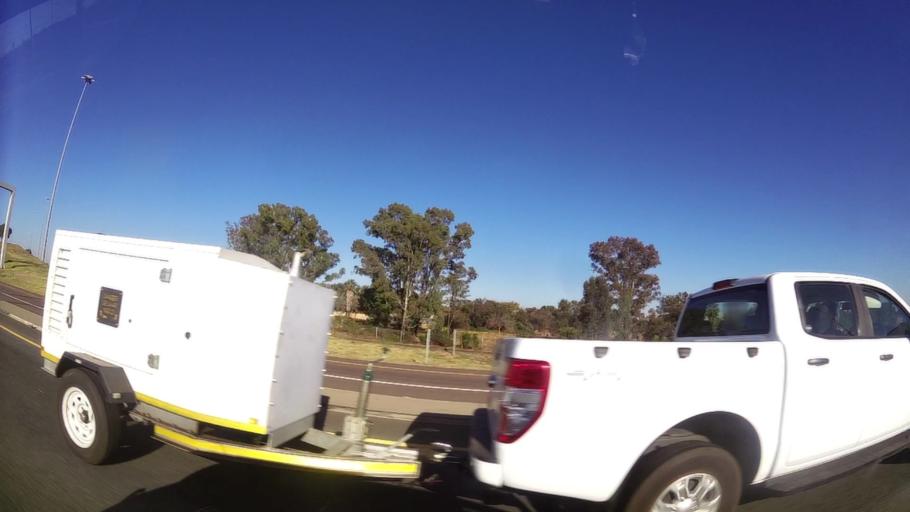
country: ZA
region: Gauteng
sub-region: City of Tshwane Metropolitan Municipality
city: Centurion
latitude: -25.8266
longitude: 28.2421
